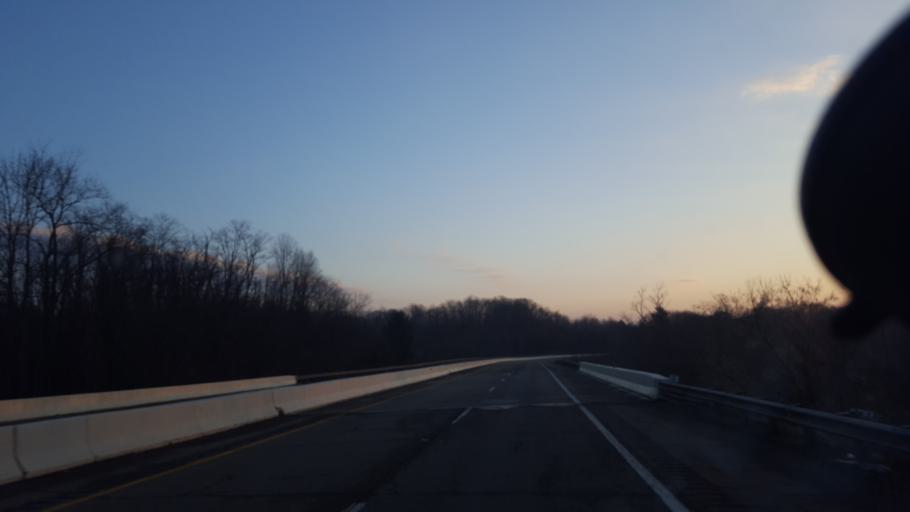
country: US
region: Ohio
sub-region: Tuscarawas County
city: Newcomerstown
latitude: 40.2835
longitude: -81.6177
